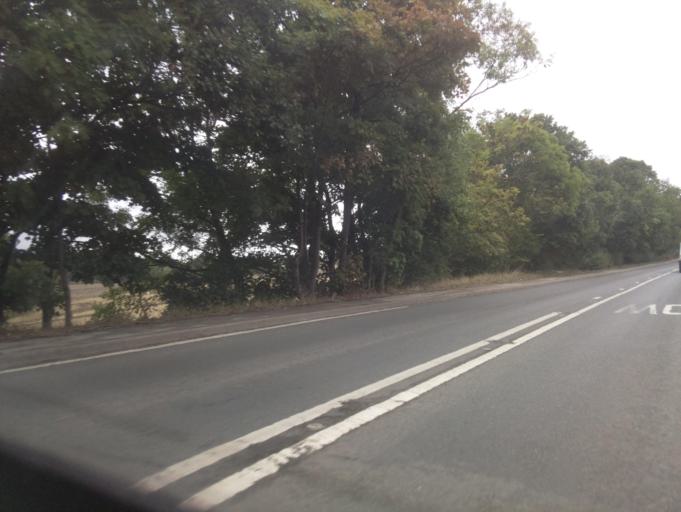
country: GB
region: England
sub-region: Kirklees
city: Clayton West
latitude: 53.6159
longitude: -1.5931
